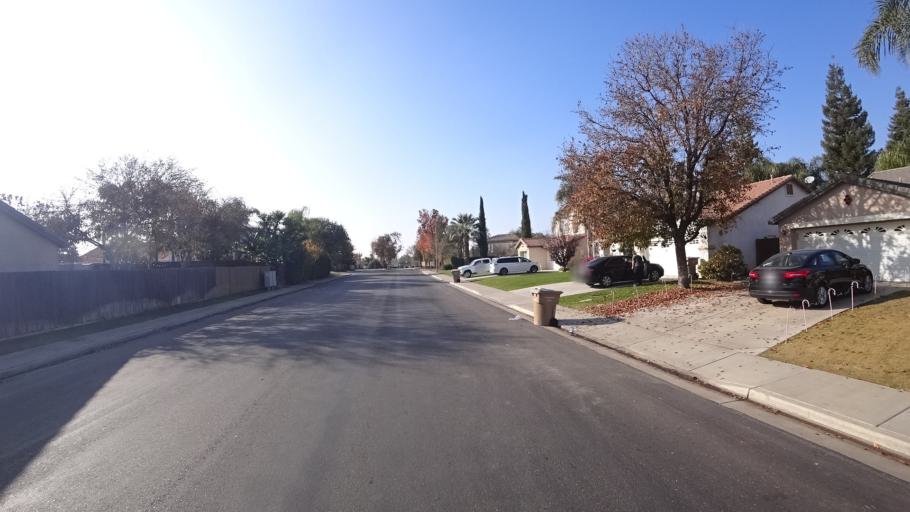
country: US
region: California
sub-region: Kern County
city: Greenacres
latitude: 35.4152
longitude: -119.0996
